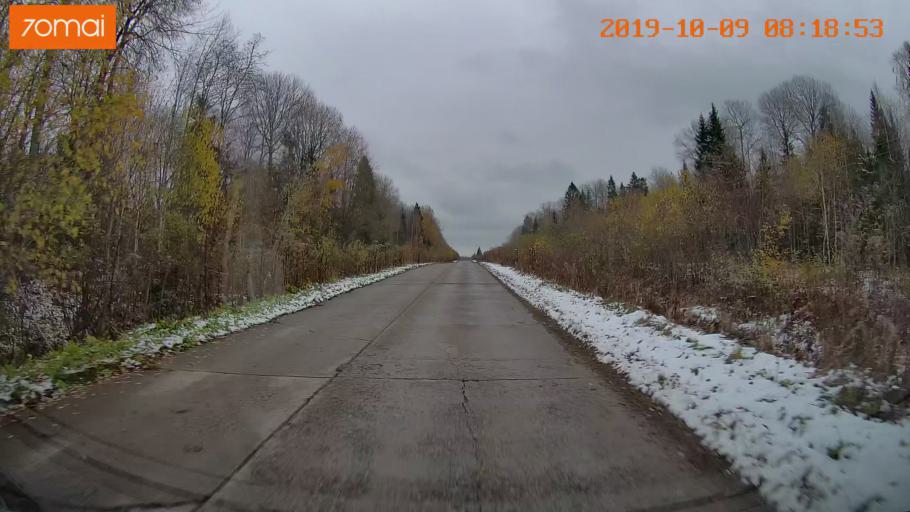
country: RU
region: Vologda
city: Gryazovets
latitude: 58.7411
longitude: 40.2316
